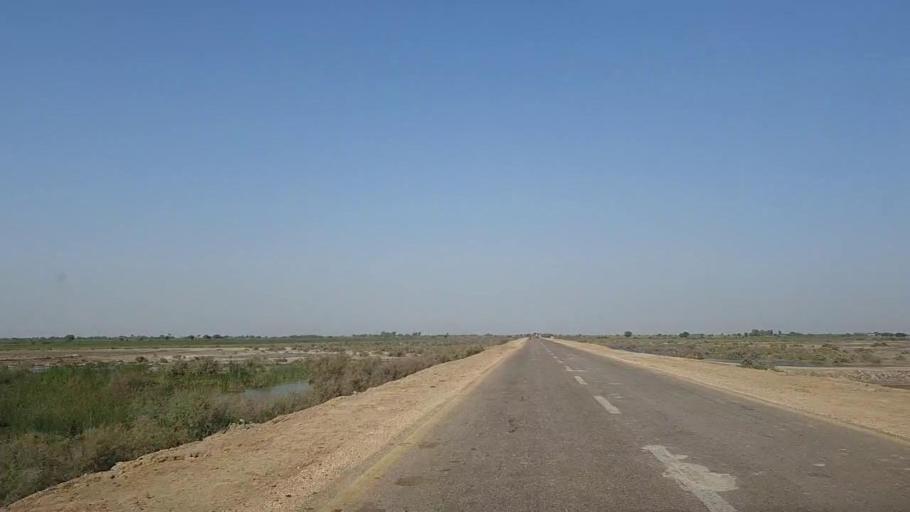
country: PK
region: Sindh
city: Jati
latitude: 24.3994
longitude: 68.2927
